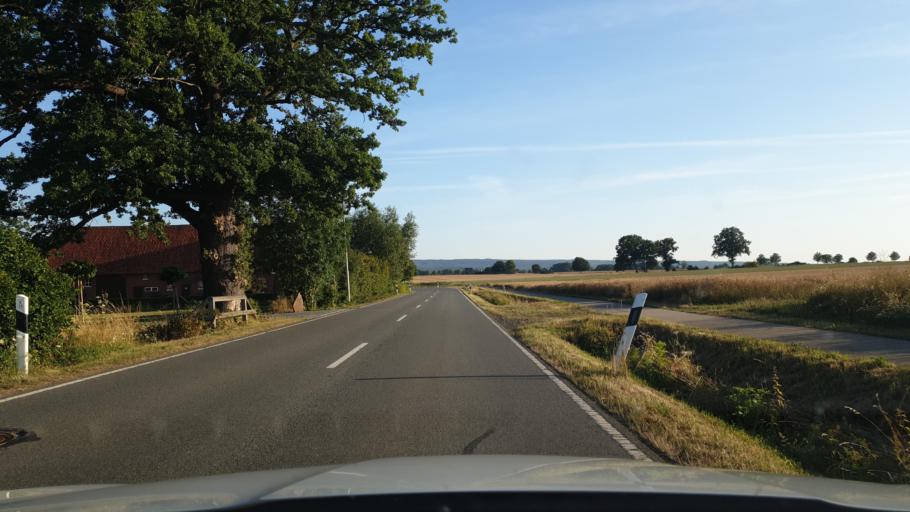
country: DE
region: Lower Saxony
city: Heuerssen
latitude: 52.3271
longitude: 9.2483
